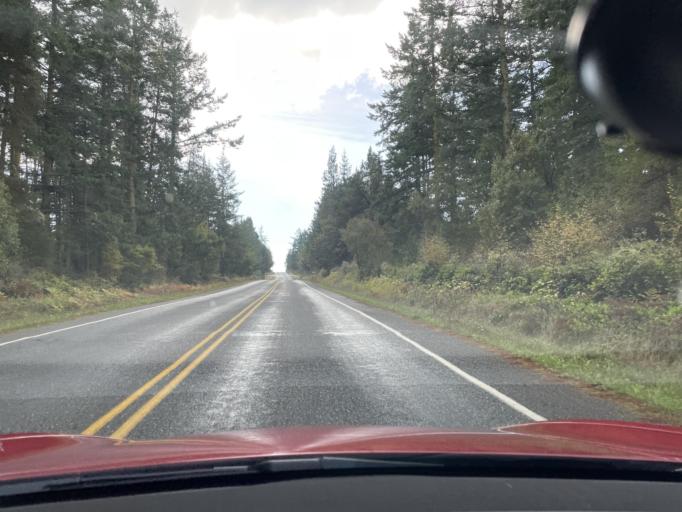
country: US
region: Washington
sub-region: San Juan County
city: Friday Harbor
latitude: 48.4882
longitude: -123.0313
